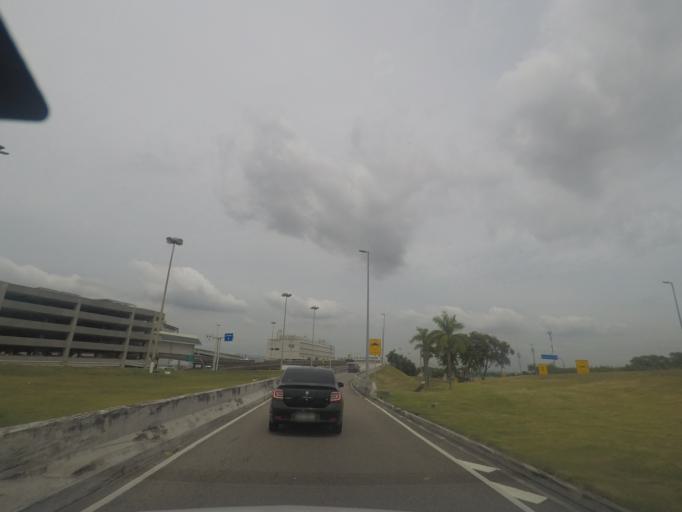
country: BR
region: Rio de Janeiro
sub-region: Duque De Caxias
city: Duque de Caxias
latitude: -22.8130
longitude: -43.2450
